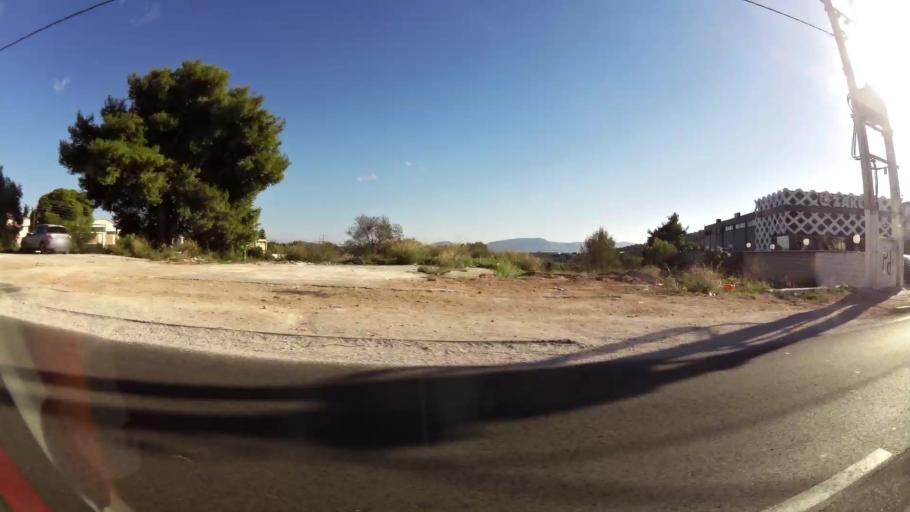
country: GR
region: Attica
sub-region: Nomarchia Anatolikis Attikis
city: Pikermi
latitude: 37.9993
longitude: 23.9345
